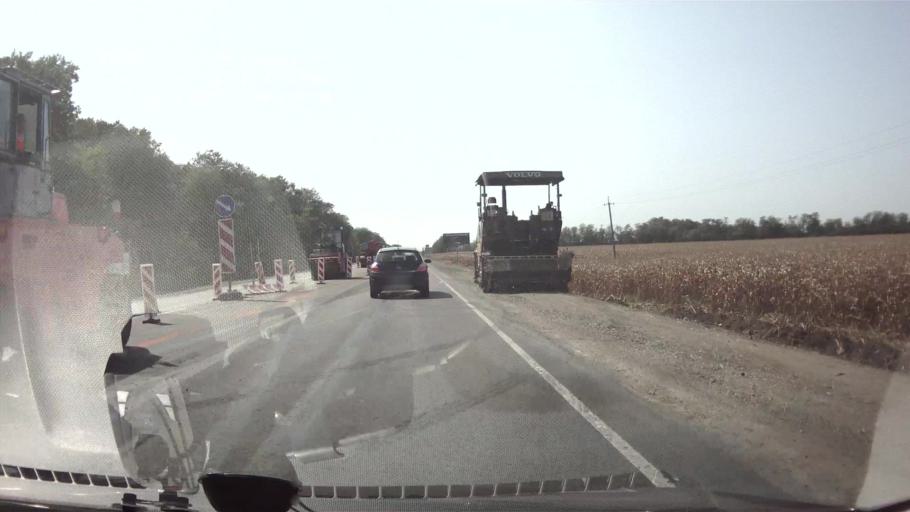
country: RU
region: Krasnodarskiy
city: Vasyurinskaya
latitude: 45.1530
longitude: 39.4469
